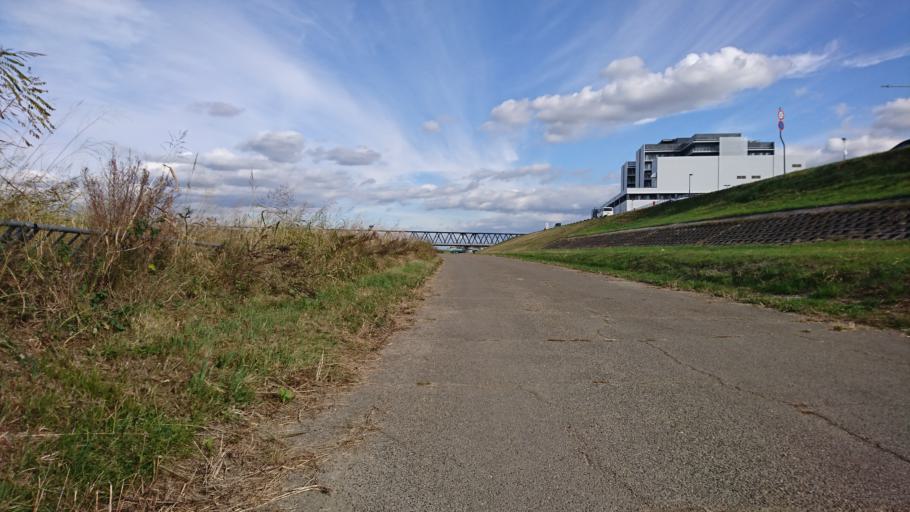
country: JP
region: Hyogo
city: Kakogawacho-honmachi
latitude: 34.7714
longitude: 134.8294
